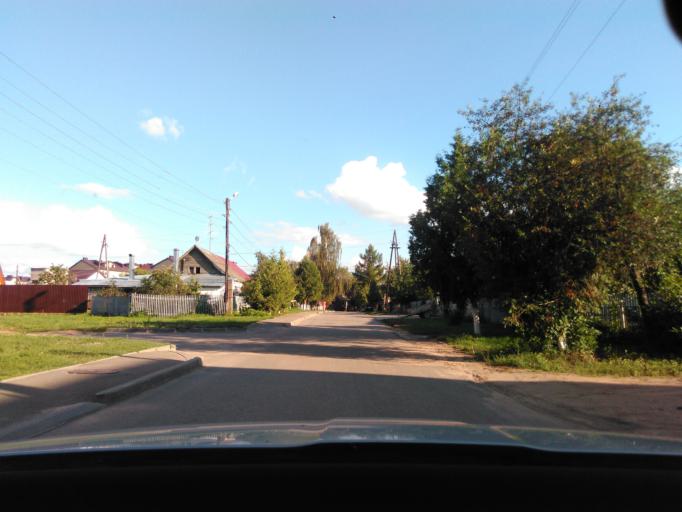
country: RU
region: Tverskaya
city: Zavidovo
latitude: 56.5803
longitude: 36.4986
